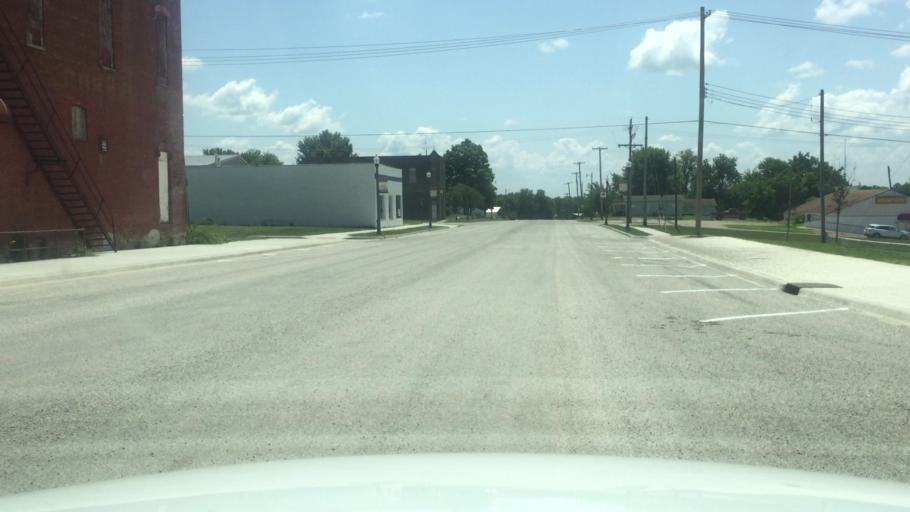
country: US
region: Kansas
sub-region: Brown County
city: Horton
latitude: 39.6600
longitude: -95.5274
